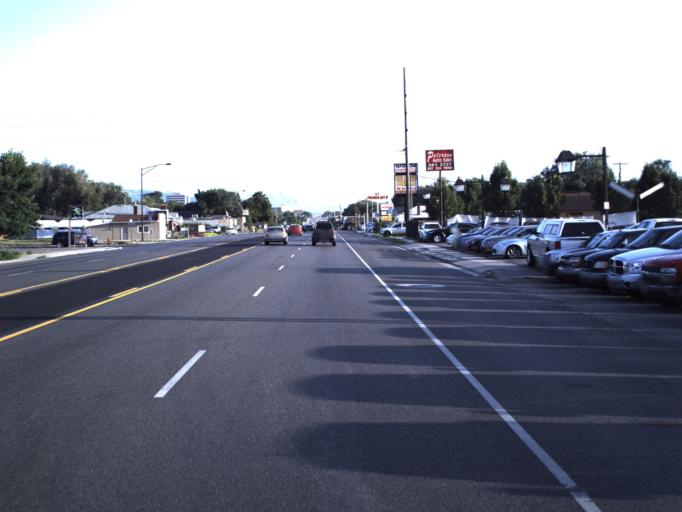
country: US
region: Utah
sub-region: Salt Lake County
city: Sandy City
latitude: 40.5972
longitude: -111.8909
